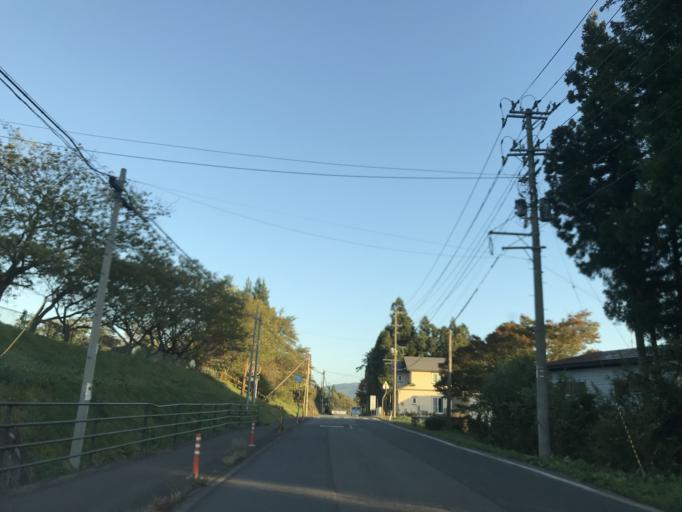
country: JP
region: Iwate
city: Mizusawa
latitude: 39.0612
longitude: 141.1069
